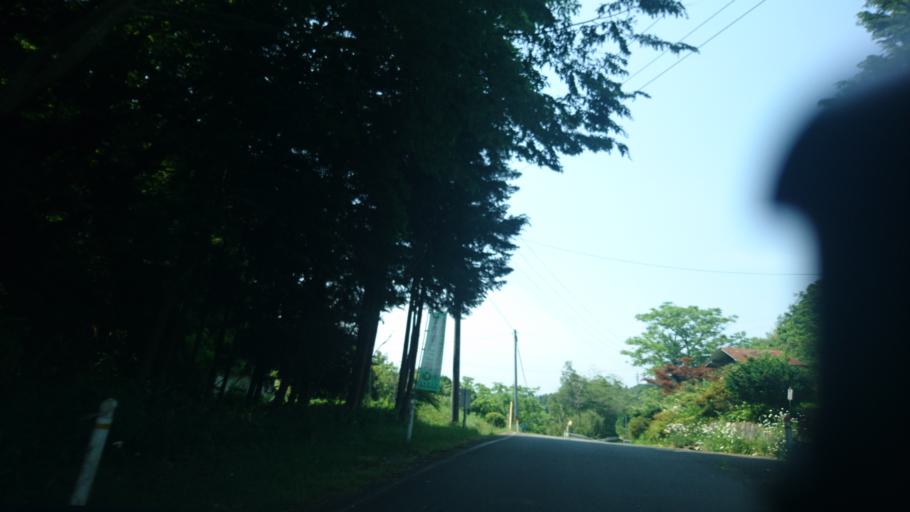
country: JP
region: Iwate
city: Ichinoseki
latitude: 38.9032
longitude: 141.3376
